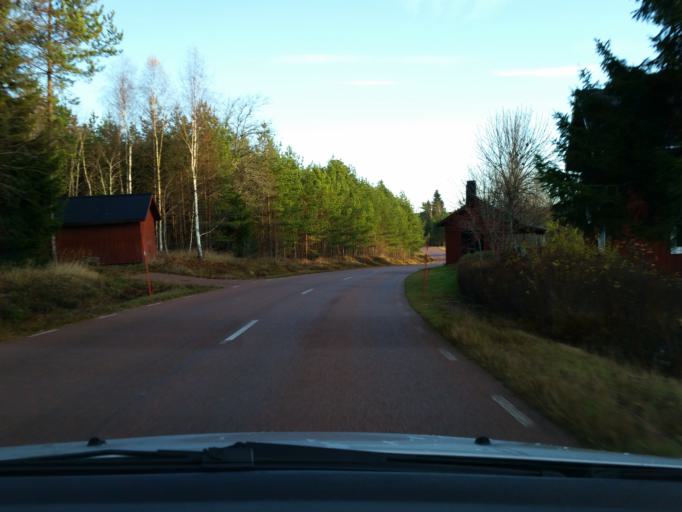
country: AX
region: Alands landsbygd
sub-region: Sund
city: Sund
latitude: 60.3057
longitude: 20.1553
